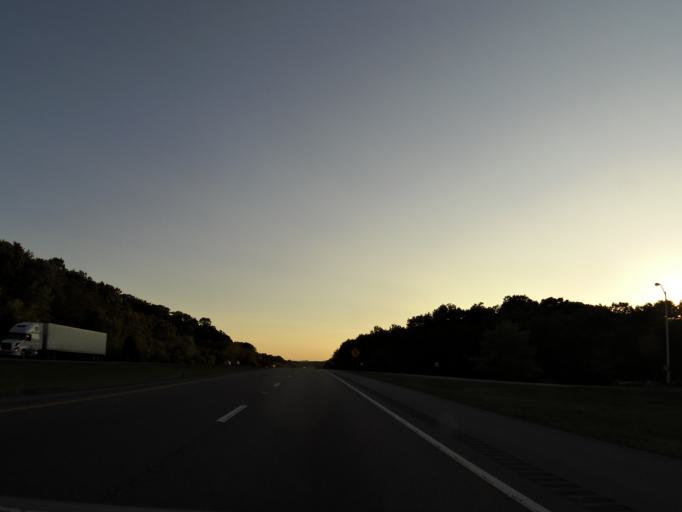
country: US
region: Tennessee
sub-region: Hawkins County
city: Surgoinsville
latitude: 36.3492
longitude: -82.7716
